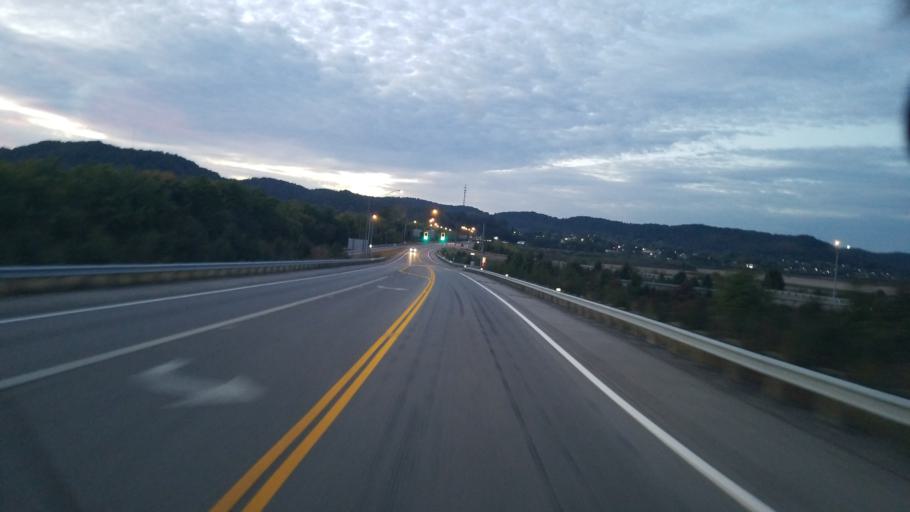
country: US
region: Ohio
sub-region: Scioto County
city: West Portsmouth
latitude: 38.7383
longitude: -83.0218
